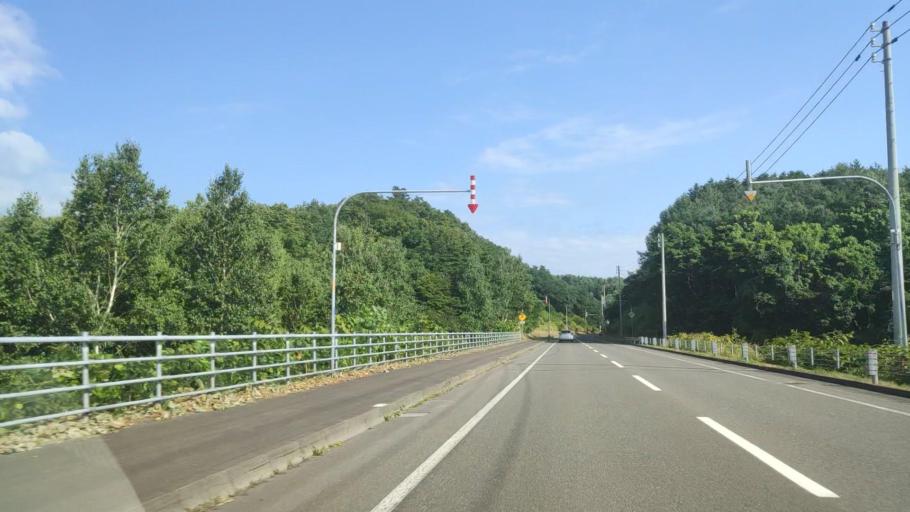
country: JP
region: Hokkaido
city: Ishikari
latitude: 43.6374
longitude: 141.3596
